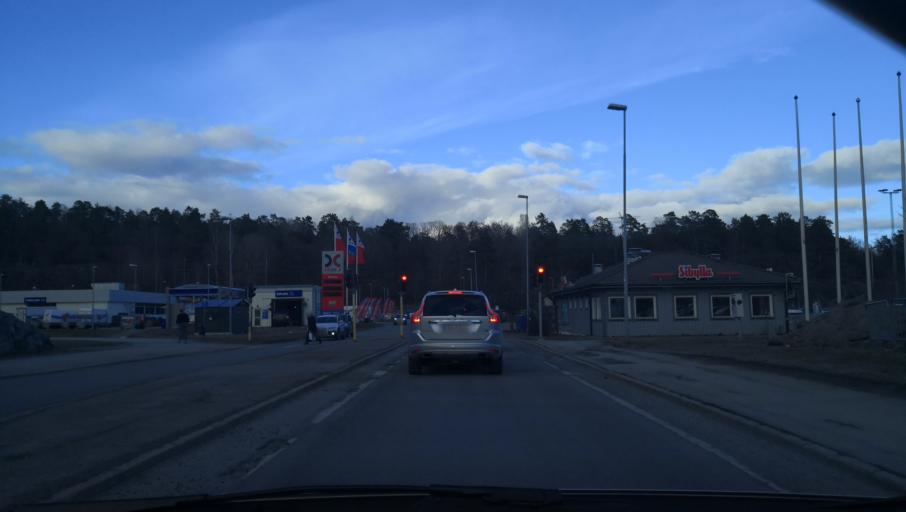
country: SE
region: Stockholm
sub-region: Varmdo Kommun
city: Gustavsberg
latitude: 59.3276
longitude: 18.3914
